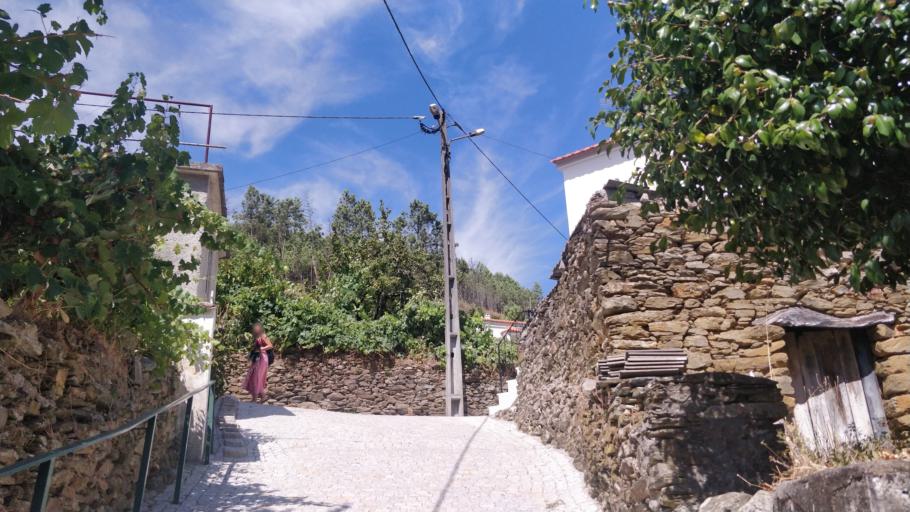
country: PT
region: Guarda
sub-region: Seia
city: Seia
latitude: 40.2854
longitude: -7.7213
